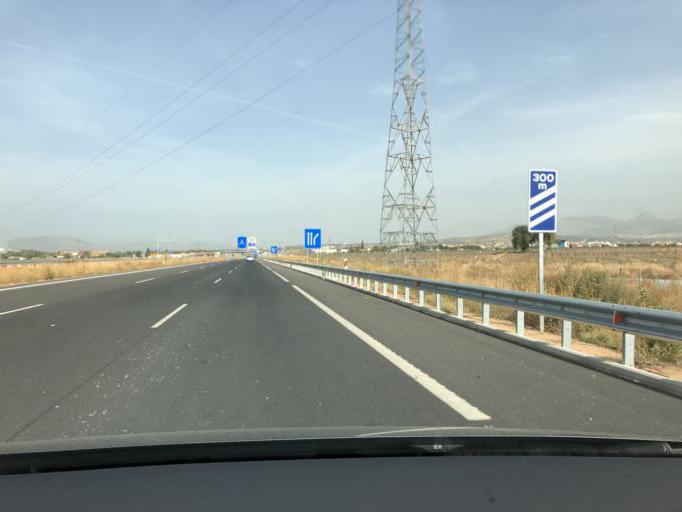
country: ES
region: Andalusia
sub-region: Provincia de Granada
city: Atarfe
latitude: 37.2184
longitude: -3.6705
